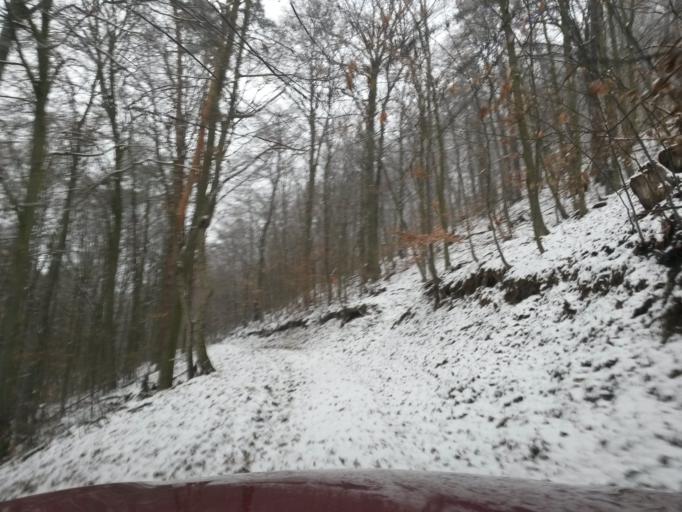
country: SK
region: Presovsky
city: Sabinov
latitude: 48.9727
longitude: 21.0902
